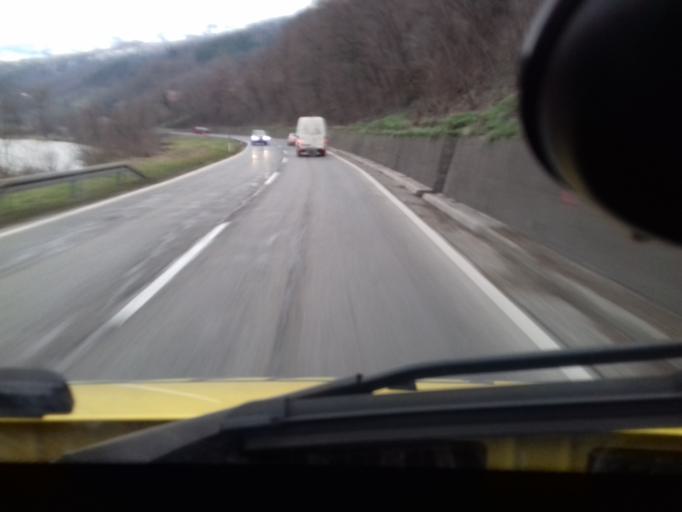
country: BA
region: Federation of Bosnia and Herzegovina
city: Zeljezno Polje
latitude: 44.3554
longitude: 17.9587
